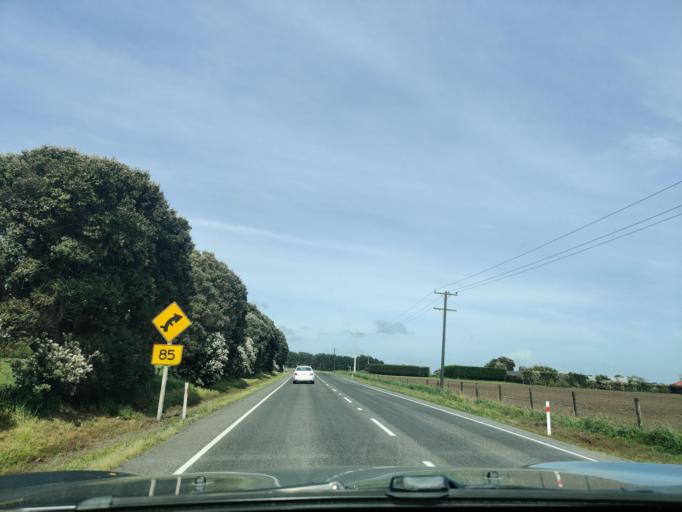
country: NZ
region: Taranaki
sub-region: South Taranaki District
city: Patea
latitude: -39.6632
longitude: 174.3992
